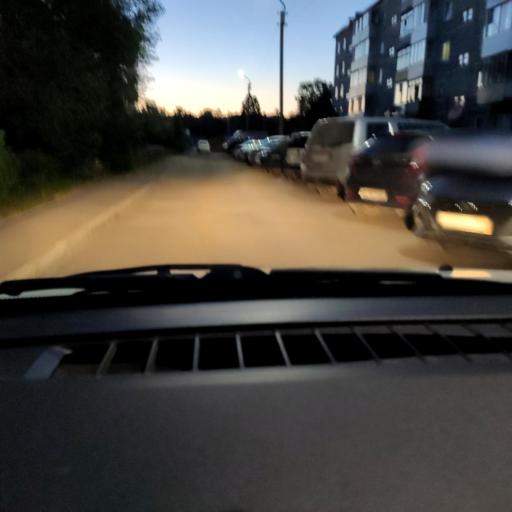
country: RU
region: Perm
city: Zvezdnyy
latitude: 57.7382
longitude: 56.3183
